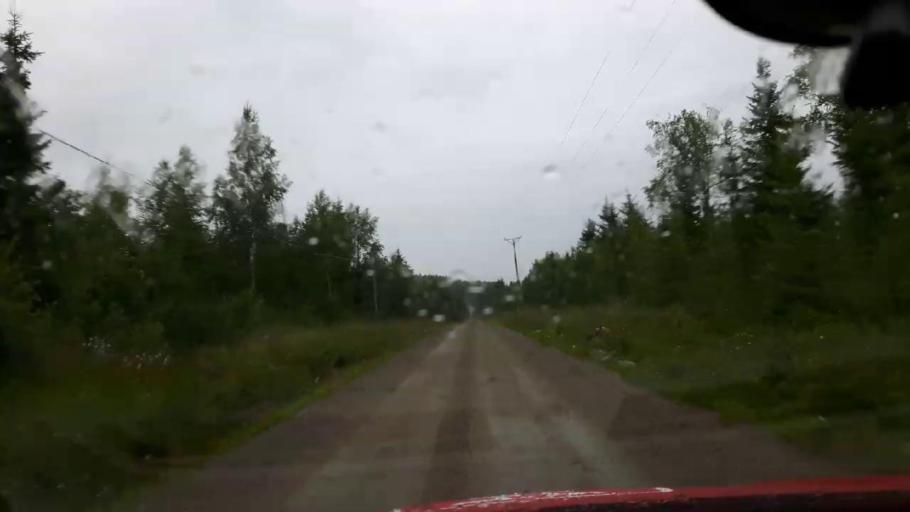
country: SE
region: Jaemtland
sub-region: OEstersunds Kommun
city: Brunflo
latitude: 62.7800
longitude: 14.9784
